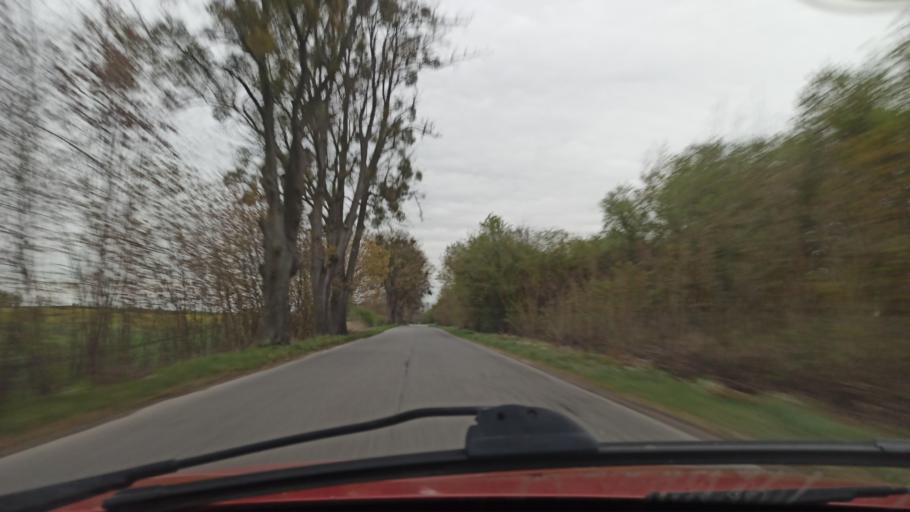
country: PL
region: Pomeranian Voivodeship
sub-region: Powiat kwidzynski
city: Gardeja
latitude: 53.5732
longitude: 18.9784
